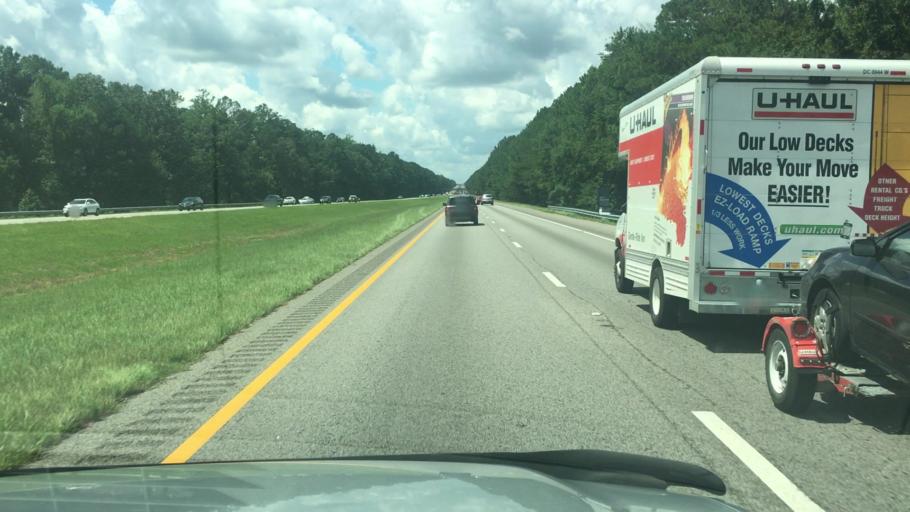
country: US
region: South Carolina
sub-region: Kershaw County
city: Elgin
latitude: 34.1350
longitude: -80.7638
